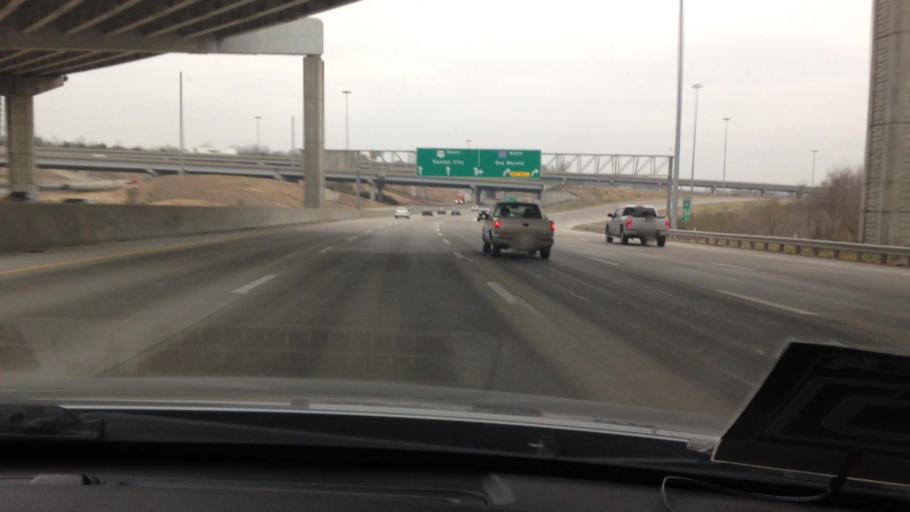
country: US
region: Missouri
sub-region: Jackson County
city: Grandview
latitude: 38.9381
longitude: -94.5346
